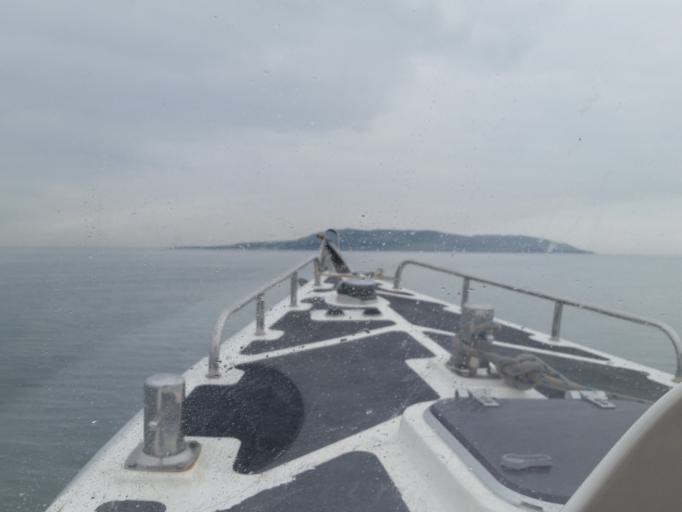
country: IE
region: Leinster
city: Portraine
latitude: 53.4759
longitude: -6.0703
